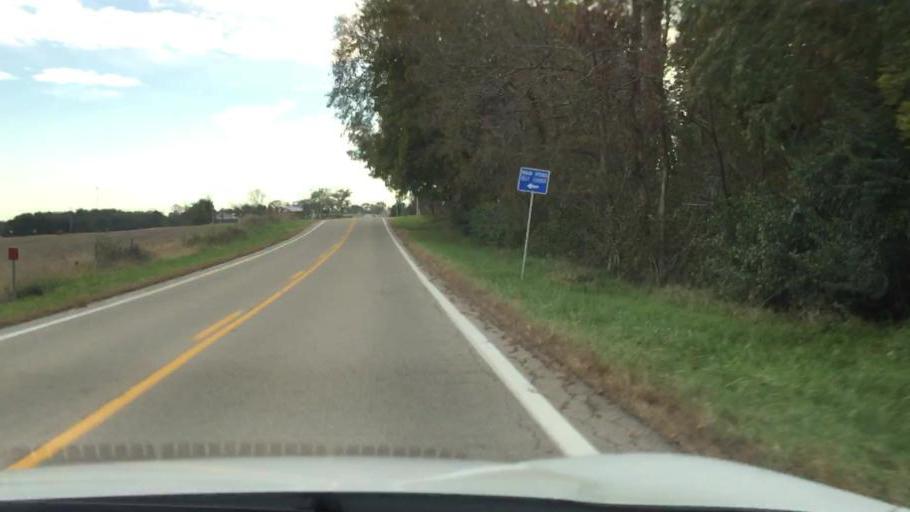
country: US
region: Ohio
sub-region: Champaign County
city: Mechanicsburg
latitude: 40.1052
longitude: -83.5409
